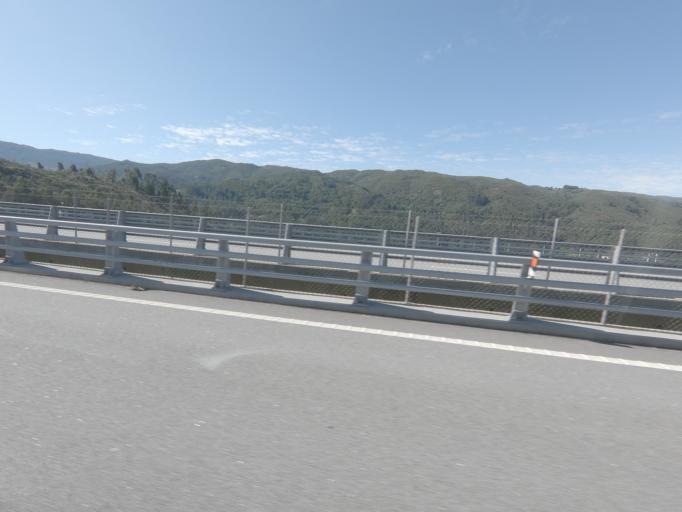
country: PT
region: Porto
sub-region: Baiao
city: Valadares
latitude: 41.2535
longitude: -7.9746
